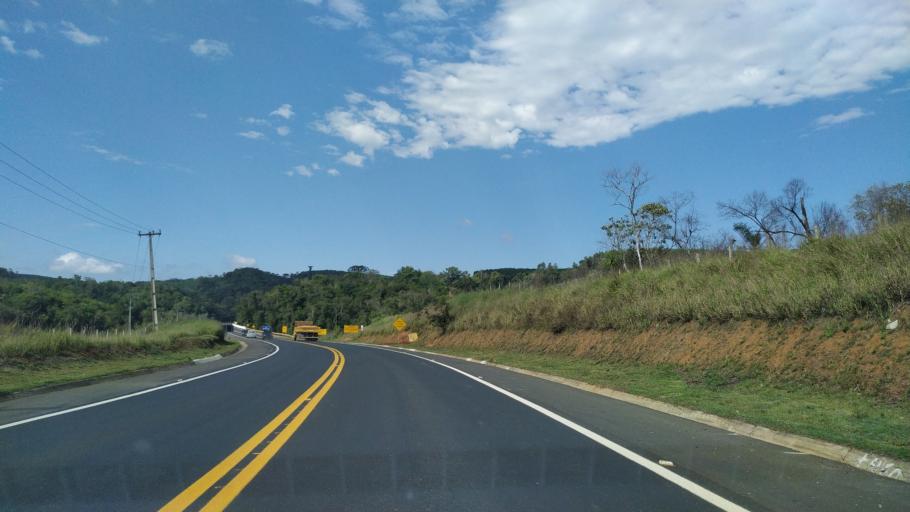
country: BR
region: Parana
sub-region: Telemaco Borba
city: Telemaco Borba
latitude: -24.2899
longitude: -50.7048
